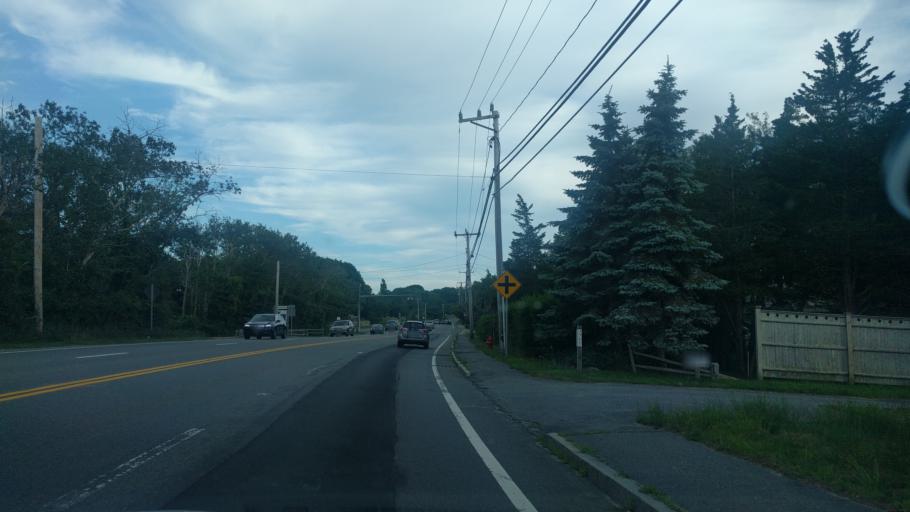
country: US
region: Massachusetts
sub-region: Barnstable County
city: Eastham
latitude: 41.8201
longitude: -69.9697
